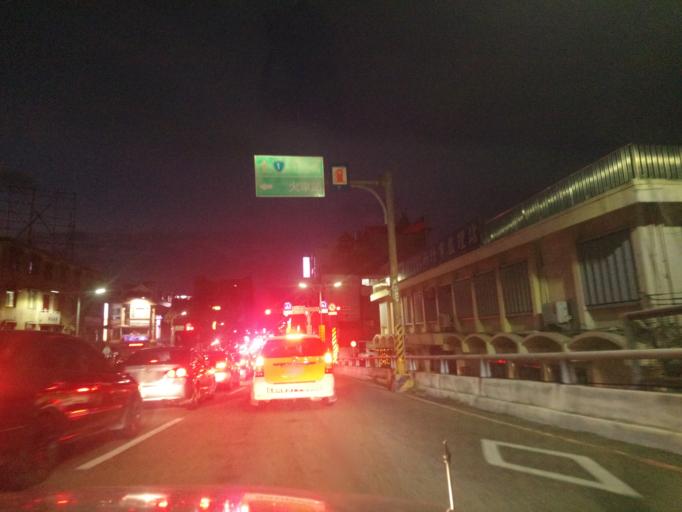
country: TW
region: Taiwan
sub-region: Hsinchu
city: Hsinchu
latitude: 24.8106
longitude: 120.9828
